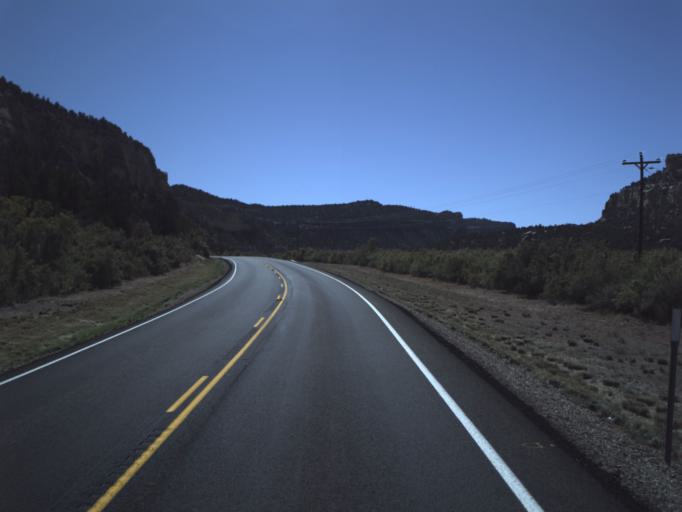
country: US
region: Utah
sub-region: Wayne County
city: Loa
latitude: 37.7547
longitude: -111.7010
